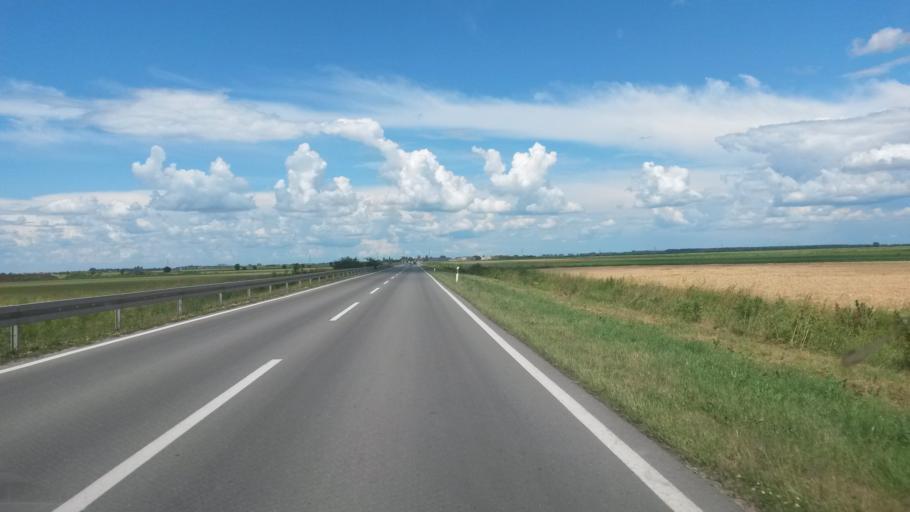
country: HR
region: Osjecko-Baranjska
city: Ovcara
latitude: 45.4793
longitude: 18.5395
